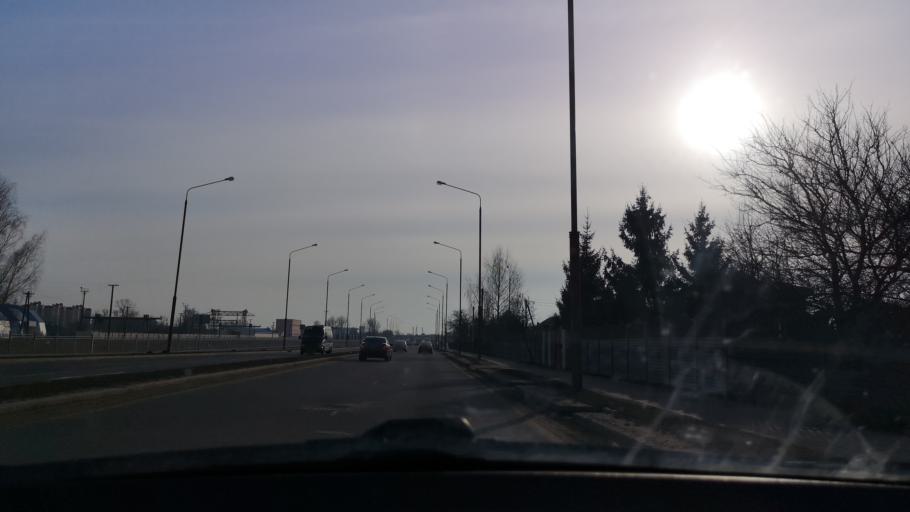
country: BY
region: Brest
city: Brest
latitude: 52.1149
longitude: 23.6689
